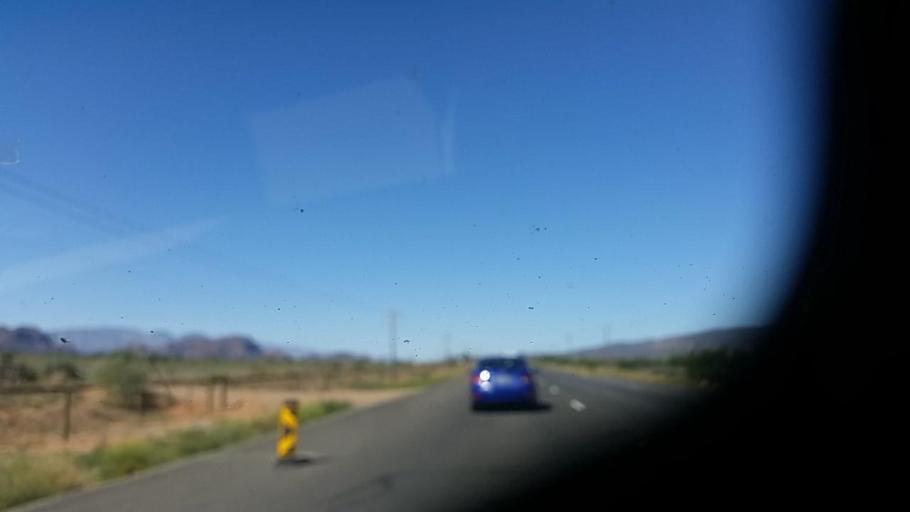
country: ZA
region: Western Cape
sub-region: Eden District Municipality
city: Oudtshoorn
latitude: -33.5620
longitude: 22.3735
